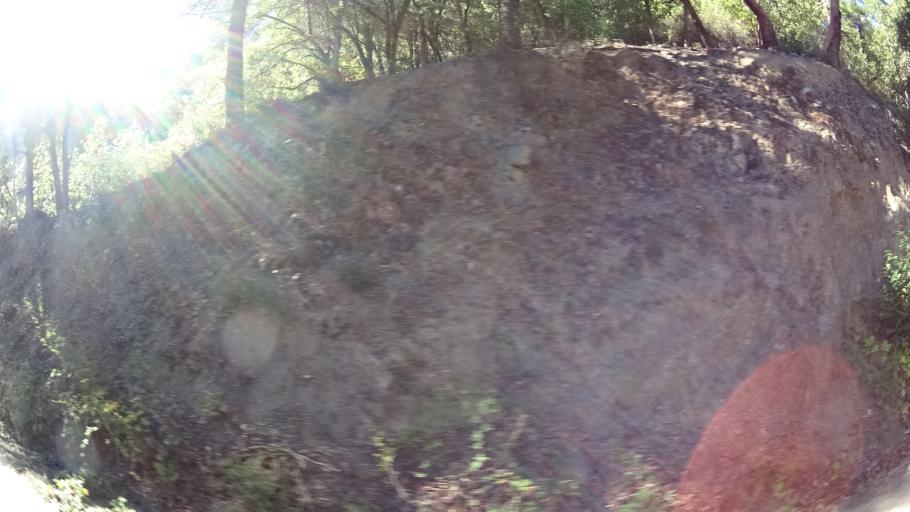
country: US
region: California
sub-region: Humboldt County
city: Willow Creek
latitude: 41.2729
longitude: -123.3026
